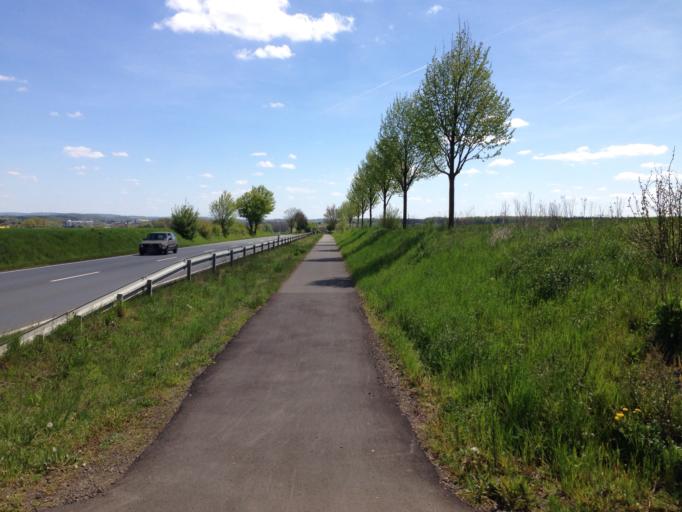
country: DE
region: Hesse
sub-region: Regierungsbezirk Giessen
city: Hungen
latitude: 50.4867
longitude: 8.8608
